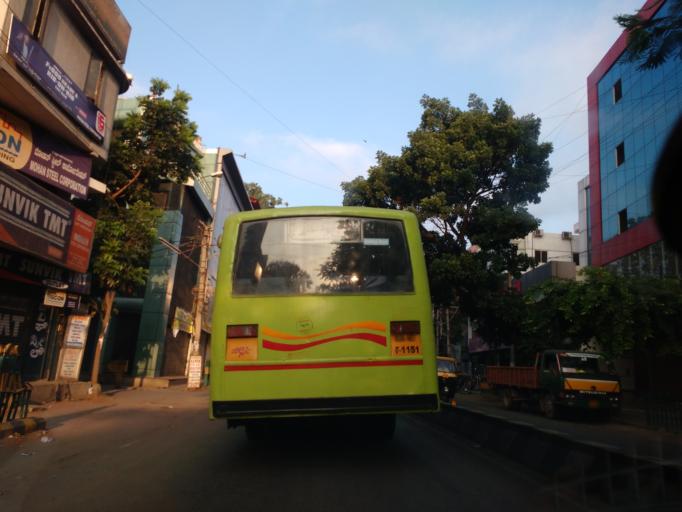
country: IN
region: Karnataka
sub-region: Bangalore Urban
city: Bangalore
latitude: 13.0044
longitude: 77.5535
